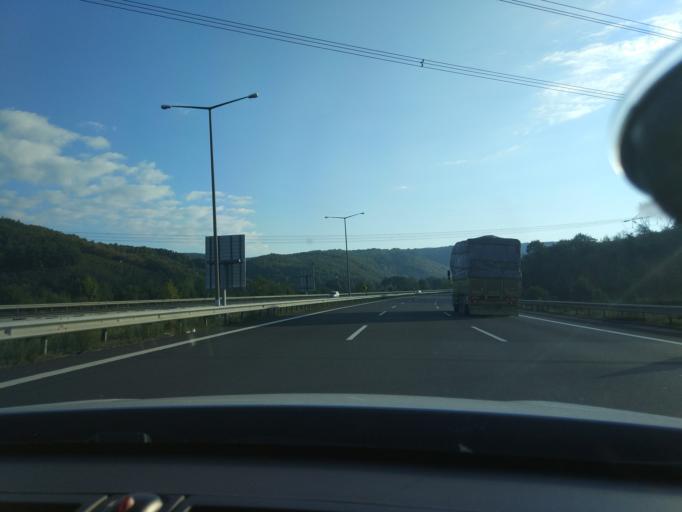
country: TR
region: Duzce
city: Kaynasli
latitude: 40.7899
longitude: 31.2817
